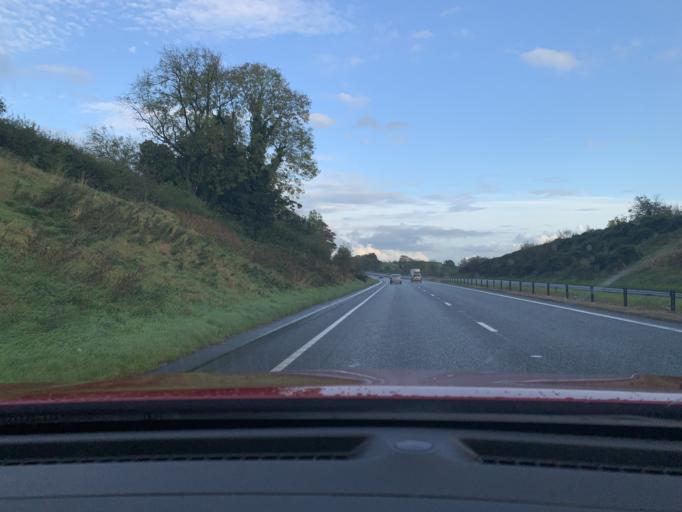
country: GB
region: Northern Ireland
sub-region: Dungannon District
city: Dungannon
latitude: 54.4779
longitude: -6.7701
